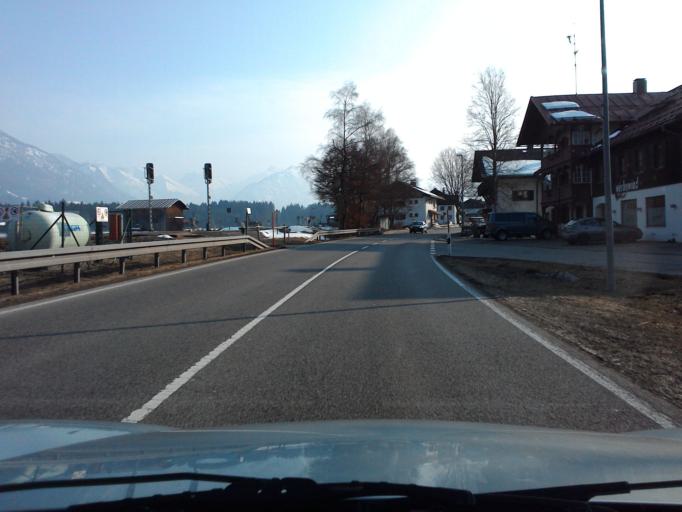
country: DE
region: Bavaria
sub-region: Swabia
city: Oberstdorf
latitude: 47.4383
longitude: 10.2758
